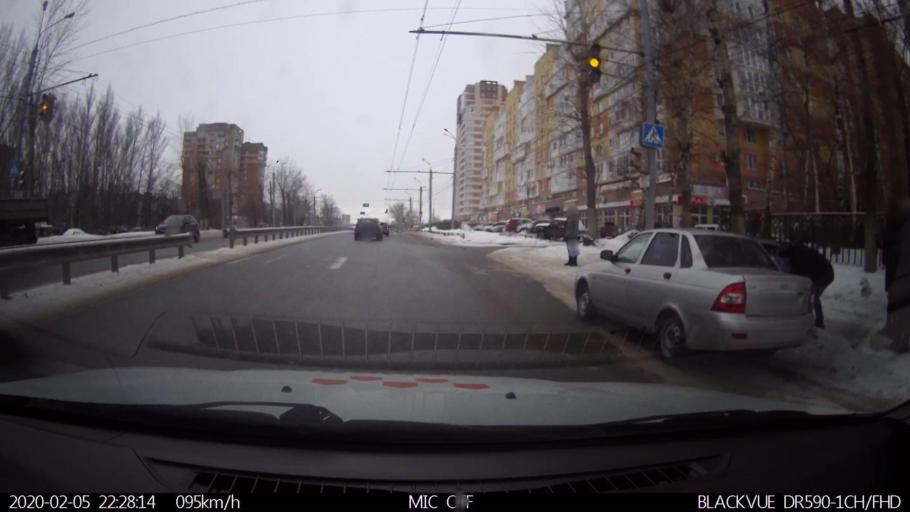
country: RU
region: Nizjnij Novgorod
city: Imeni Stepana Razina
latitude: 54.7590
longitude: 44.1293
